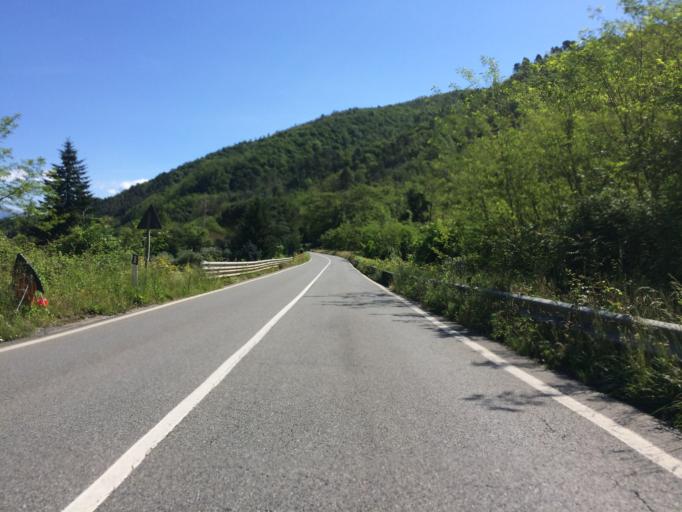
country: IT
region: Tuscany
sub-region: Provincia di Massa-Carrara
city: Albiano Magra
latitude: 44.1844
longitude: 9.9340
